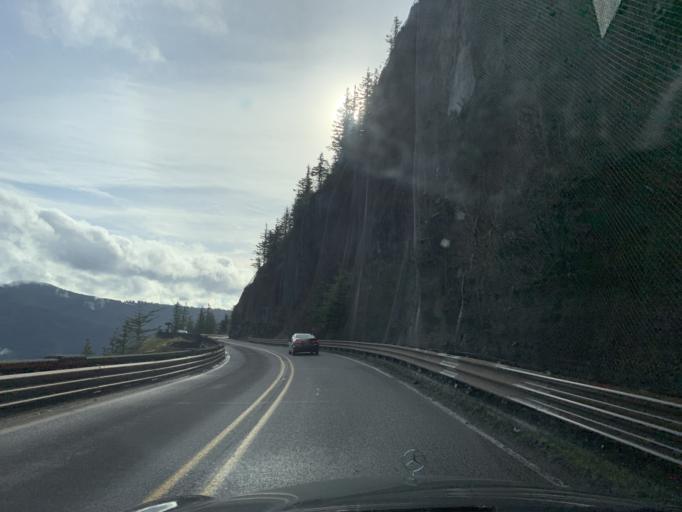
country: US
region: Washington
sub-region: Clark County
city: Washougal
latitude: 45.5773
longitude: -122.1950
